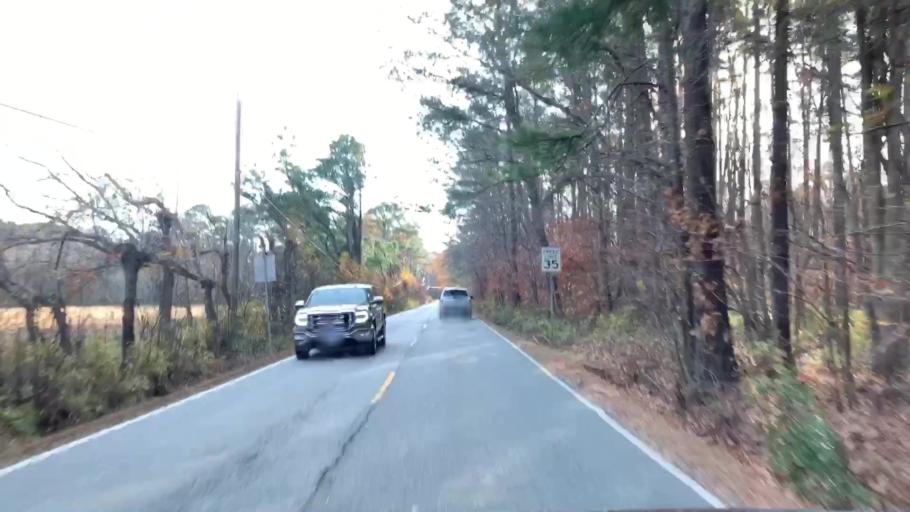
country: US
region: Virginia
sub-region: City of Virginia Beach
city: Virginia Beach
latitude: 36.7378
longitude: -76.1042
